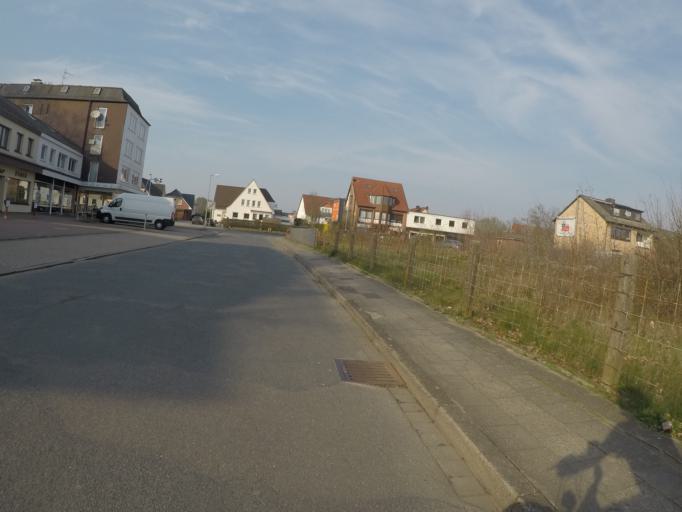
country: DE
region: Schleswig-Holstein
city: Wahlstedt
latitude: 53.9532
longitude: 10.2084
